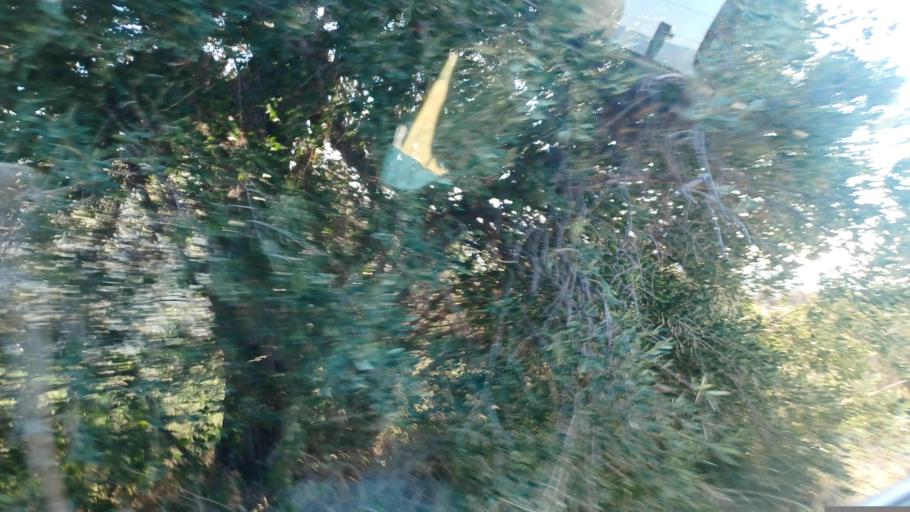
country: CY
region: Larnaka
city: Kofinou
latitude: 34.8397
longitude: 33.3023
